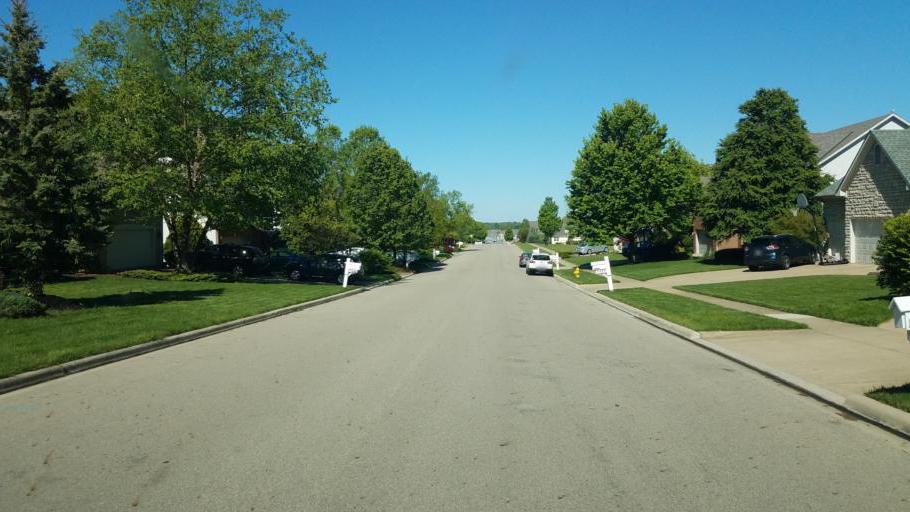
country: US
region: Ohio
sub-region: Franklin County
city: Westerville
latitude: 40.1733
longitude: -82.9389
